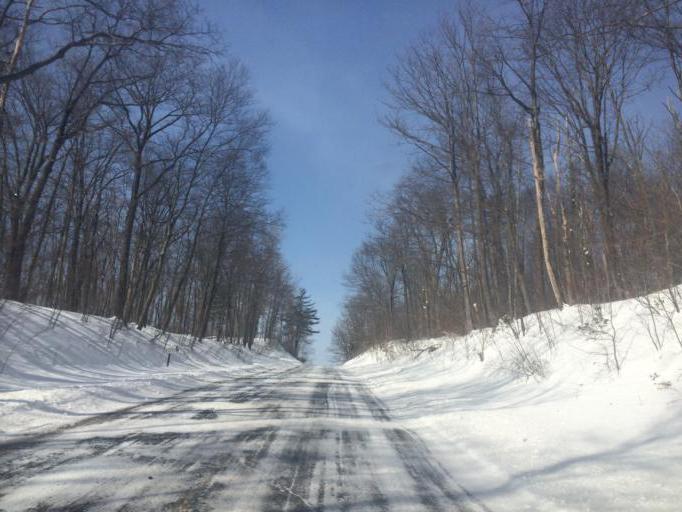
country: US
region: Pennsylvania
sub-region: Centre County
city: Stormstown
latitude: 40.8818
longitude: -78.0191
